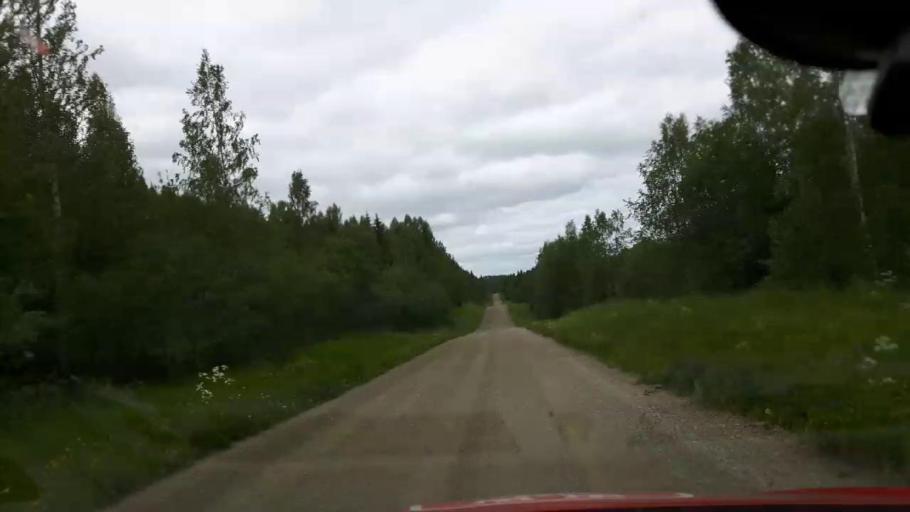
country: SE
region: Jaemtland
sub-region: OEstersunds Kommun
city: Brunflo
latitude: 62.9364
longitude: 14.9935
